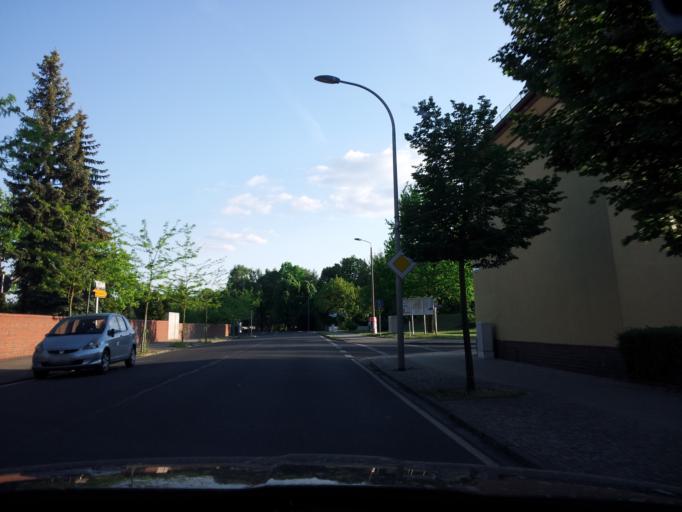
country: DE
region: Brandenburg
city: Luckenwalde
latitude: 52.0793
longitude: 13.1594
